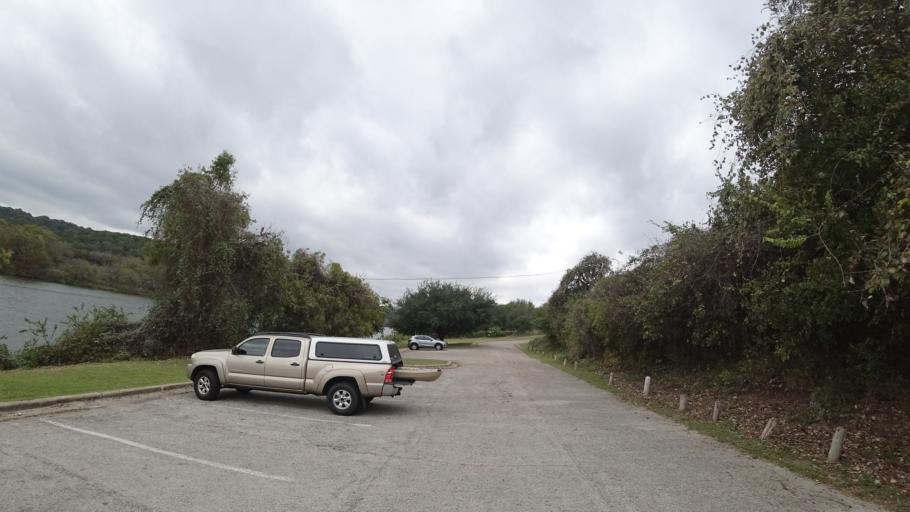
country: US
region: Texas
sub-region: Travis County
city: Bee Cave
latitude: 30.3382
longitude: -97.9033
